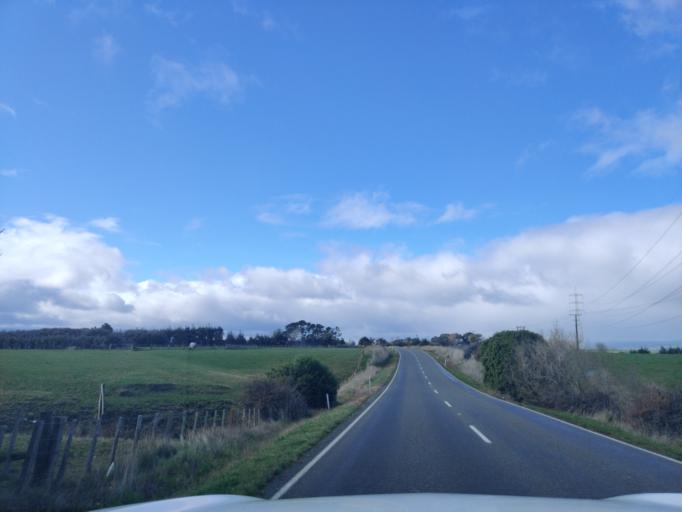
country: NZ
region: Manawatu-Wanganui
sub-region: Palmerston North City
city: Palmerston North
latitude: -40.2863
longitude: 175.6671
